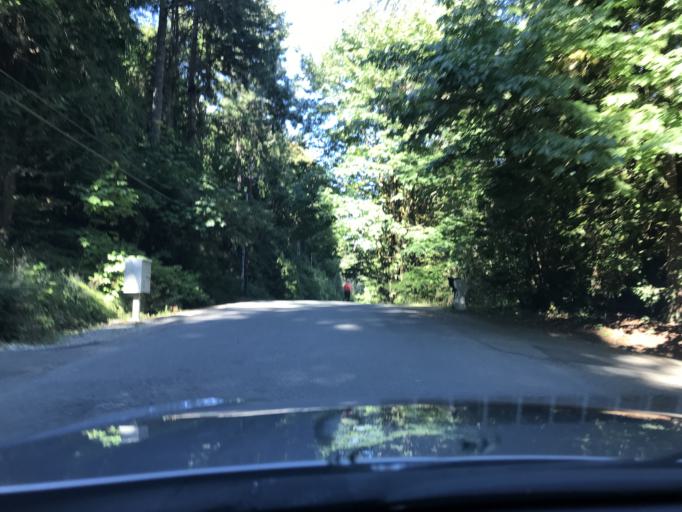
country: US
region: Washington
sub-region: King County
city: Maple Heights-Lake Desire
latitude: 47.4416
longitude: -122.0881
